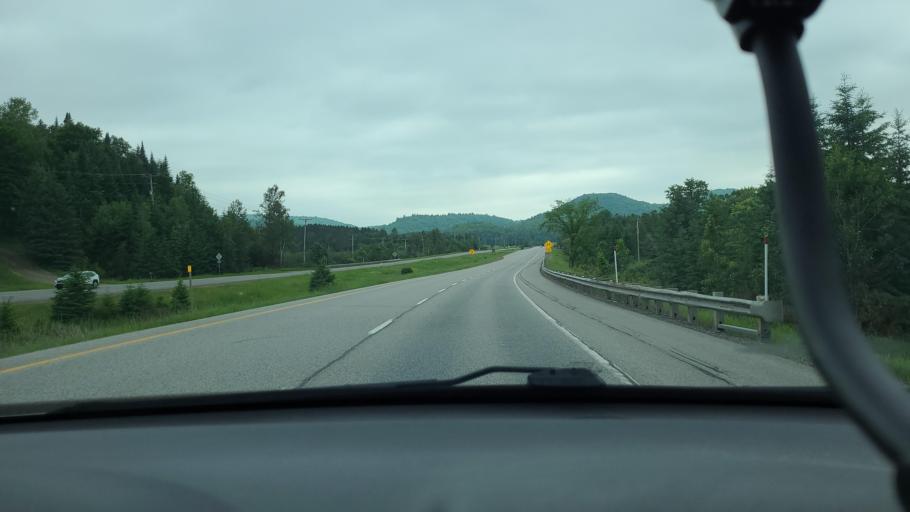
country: CA
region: Quebec
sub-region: Laurentides
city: Labelle
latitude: 46.1786
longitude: -74.7267
